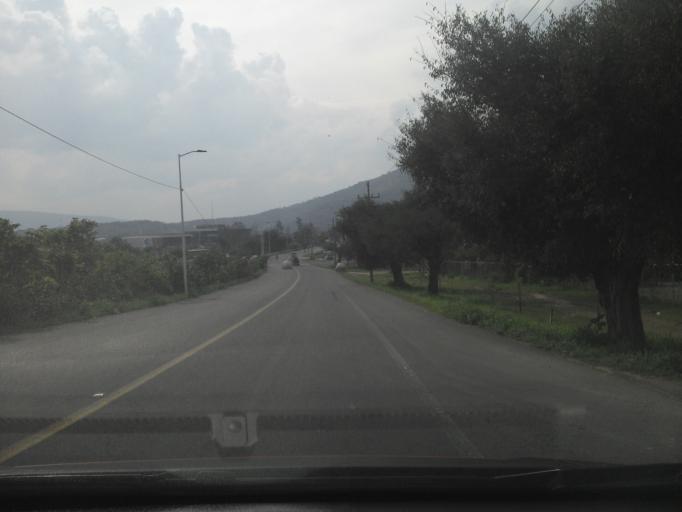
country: MX
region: Jalisco
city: Tlajomulco de Zuniga
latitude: 20.4781
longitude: -103.4372
